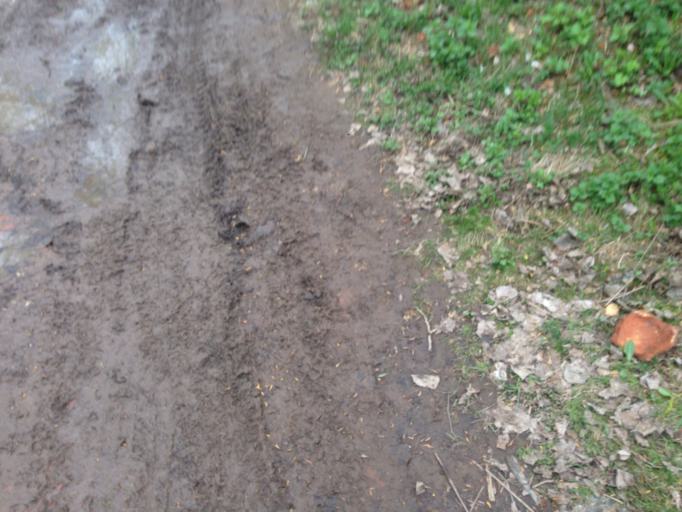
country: RU
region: Tula
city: Krapivna
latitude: 53.9387
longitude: 37.1521
